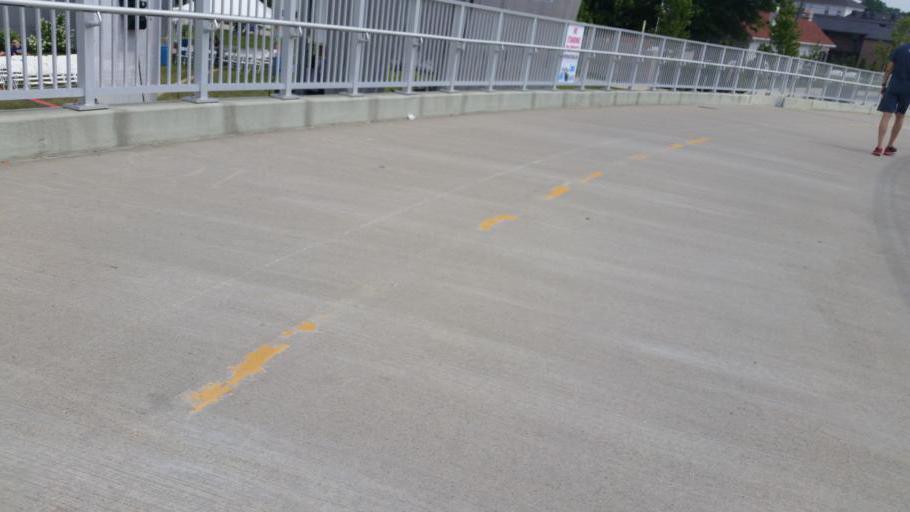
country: US
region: Indiana
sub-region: Clark County
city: Jeffersonville
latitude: 38.2706
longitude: -85.7424
